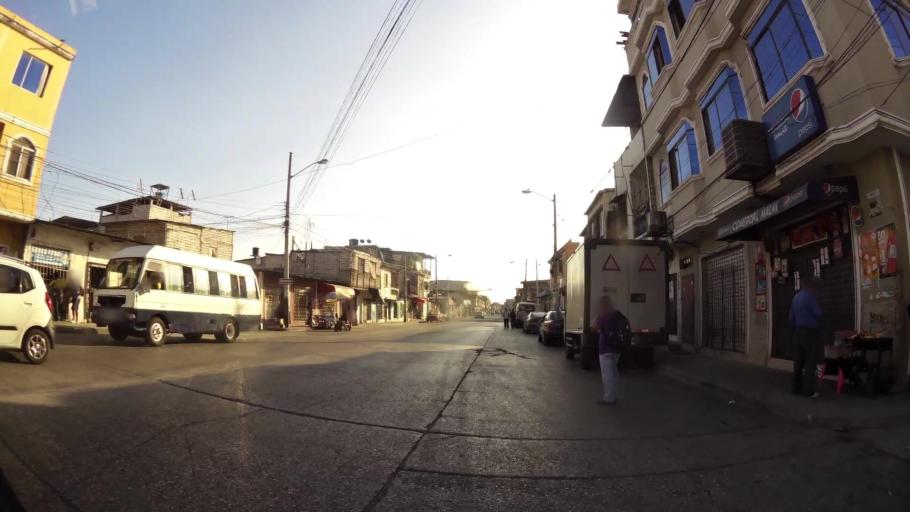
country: EC
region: Guayas
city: Guayaquil
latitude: -2.2293
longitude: -79.9078
